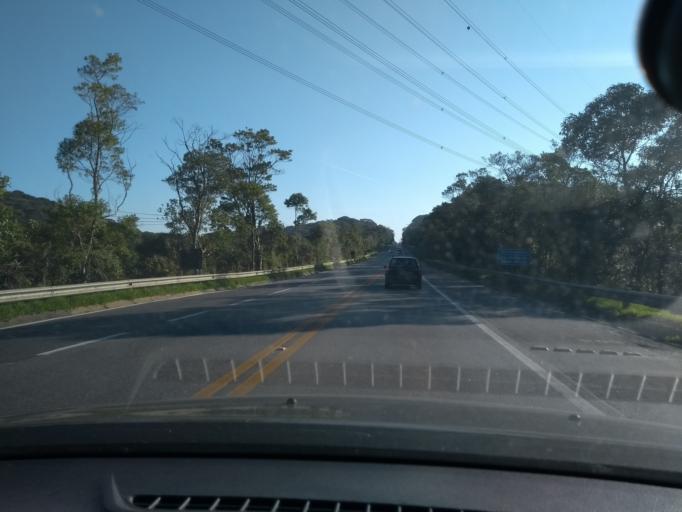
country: BR
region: Sao Paulo
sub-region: Rio Grande Da Serra
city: Rio Grande da Serra
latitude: -23.7718
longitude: -46.4747
